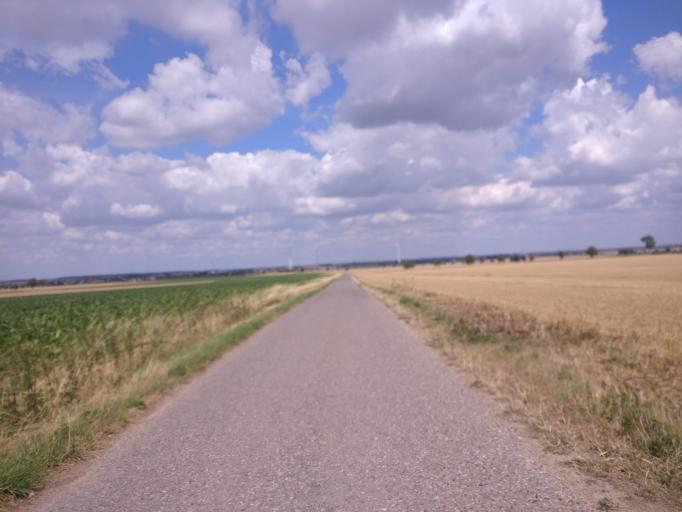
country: DE
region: Lower Saxony
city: Hildesheim
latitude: 52.1438
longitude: 10.0258
